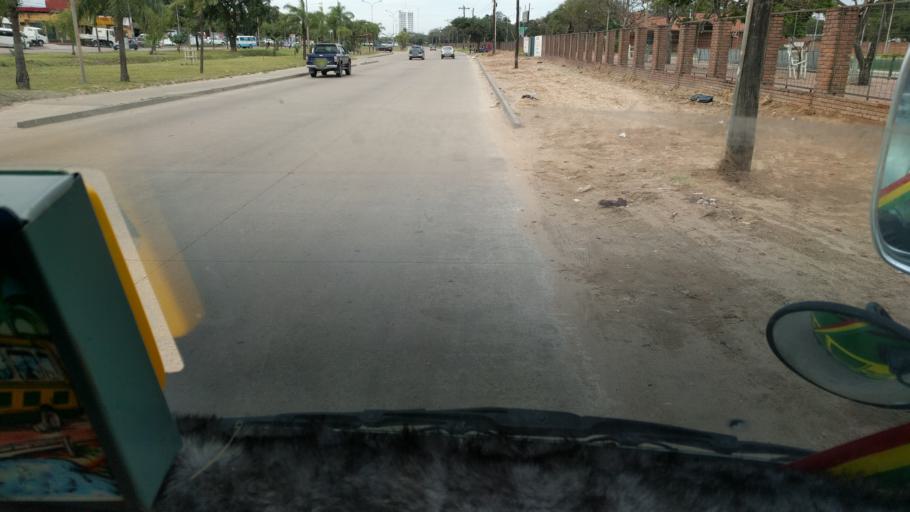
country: BO
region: Santa Cruz
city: Santa Cruz de la Sierra
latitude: -17.8214
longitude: -63.1932
